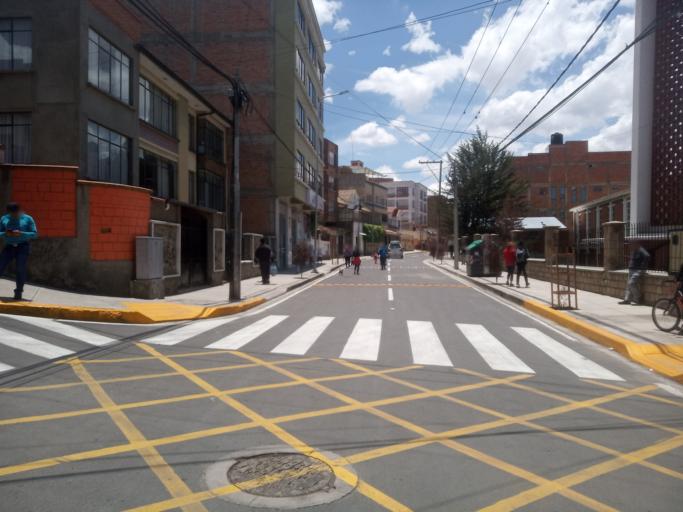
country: BO
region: La Paz
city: La Paz
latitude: -16.5111
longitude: -68.1343
